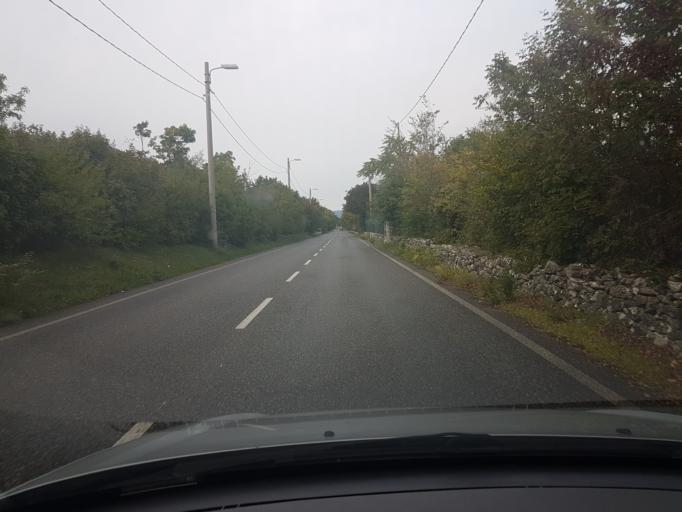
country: IT
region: Friuli Venezia Giulia
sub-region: Provincia di Trieste
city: Santa Croce
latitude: 45.7405
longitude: 13.6857
